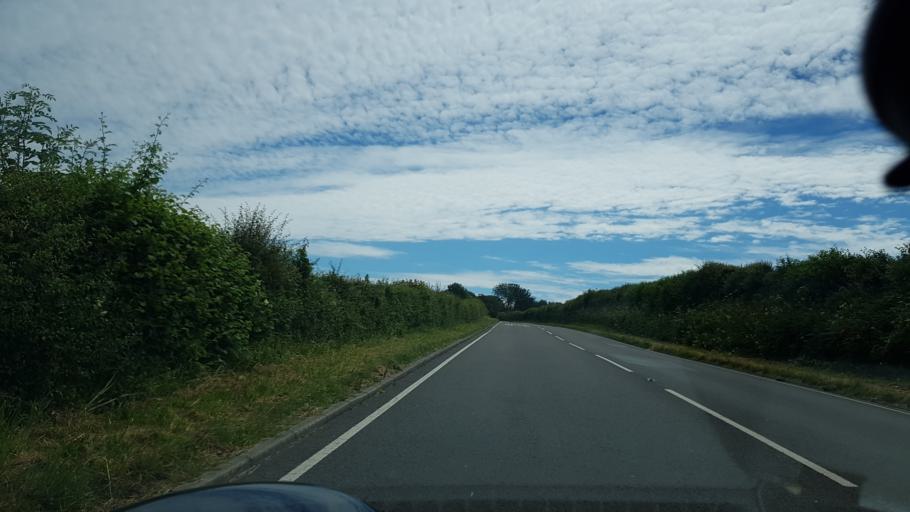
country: GB
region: Wales
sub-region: Carmarthenshire
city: Saint Clears
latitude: 51.7880
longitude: -4.4809
